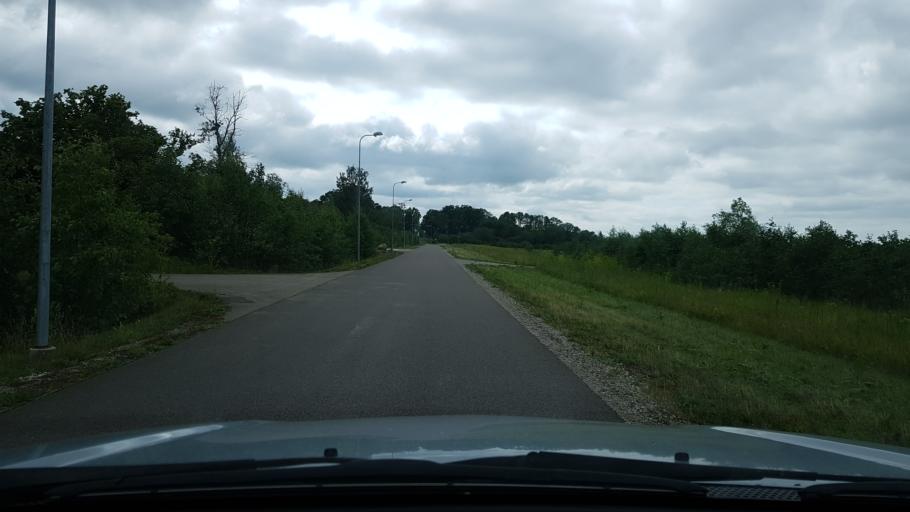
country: EE
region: Ida-Virumaa
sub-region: Narva linn
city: Narva
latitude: 59.3938
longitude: 28.1133
